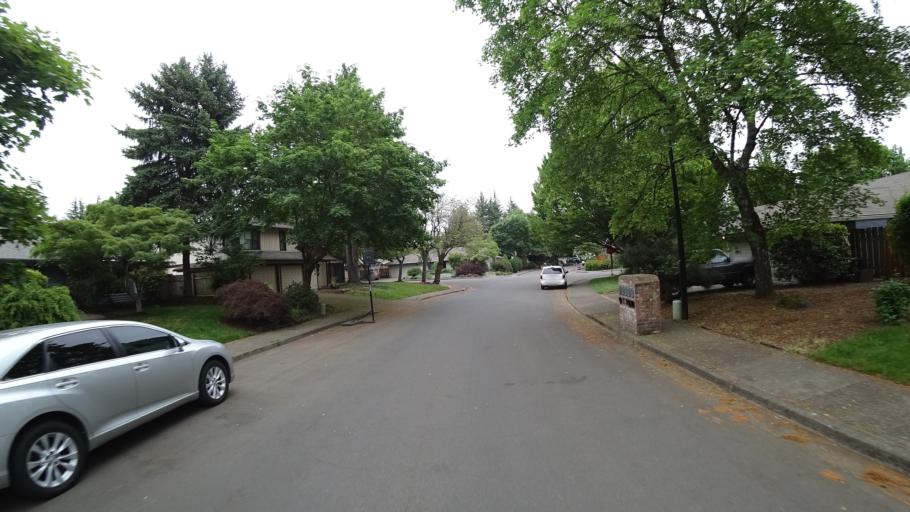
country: US
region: Oregon
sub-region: Washington County
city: Rockcreek
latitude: 45.5614
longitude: -122.8935
